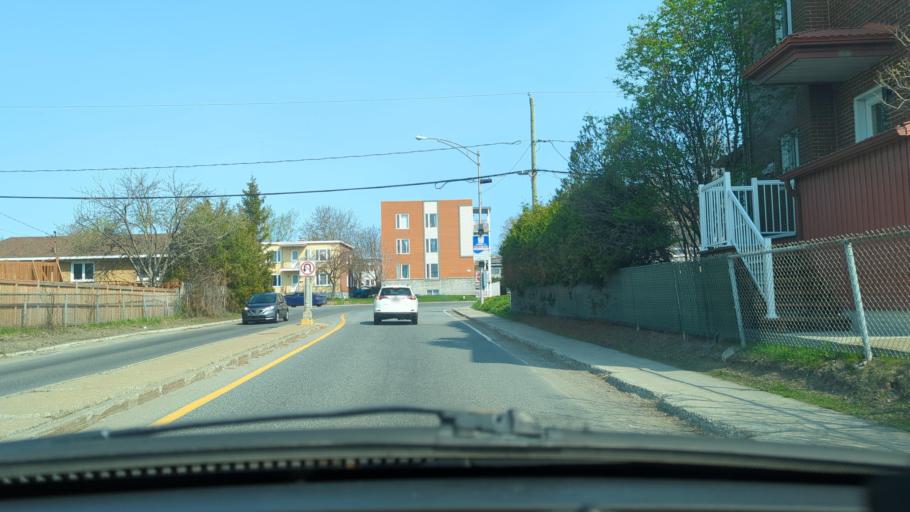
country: CA
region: Quebec
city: Quebec
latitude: 46.8458
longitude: -71.2472
